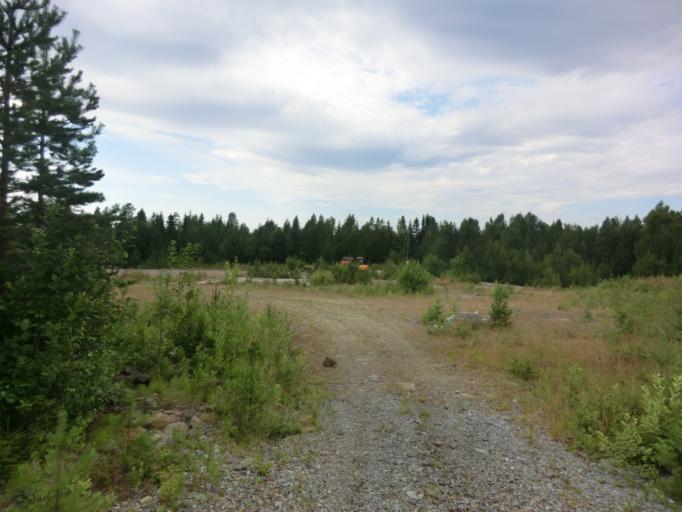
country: SE
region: Vaesterbotten
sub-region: Lycksele Kommun
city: Lycksele
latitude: 64.0801
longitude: 18.3502
